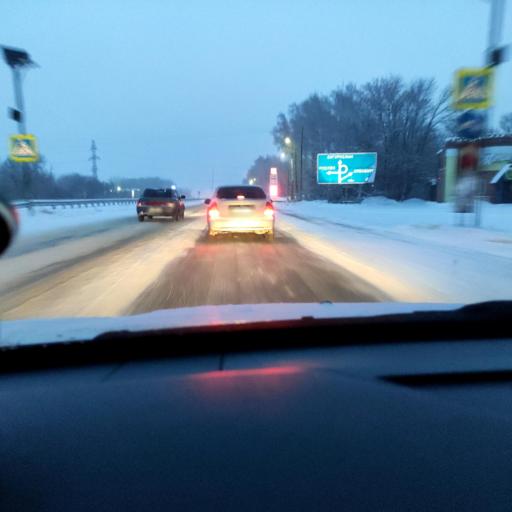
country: RU
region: Samara
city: Smyshlyayevka
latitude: 53.2596
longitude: 50.4574
